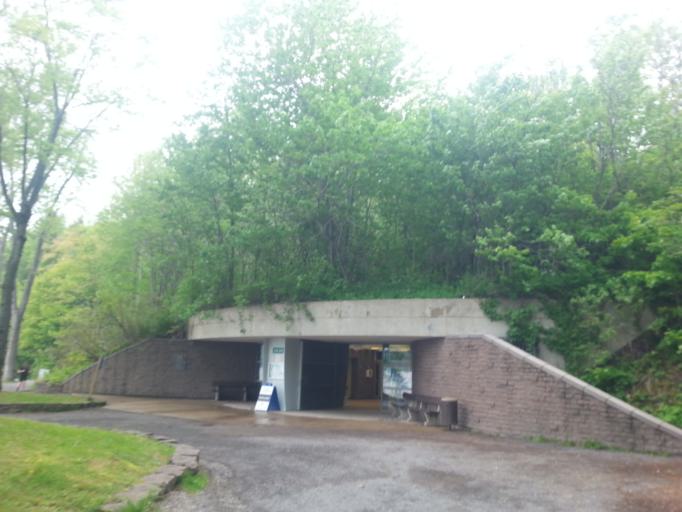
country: CA
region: Quebec
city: L'Ancienne-Lorette
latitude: 46.7505
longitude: -71.3154
